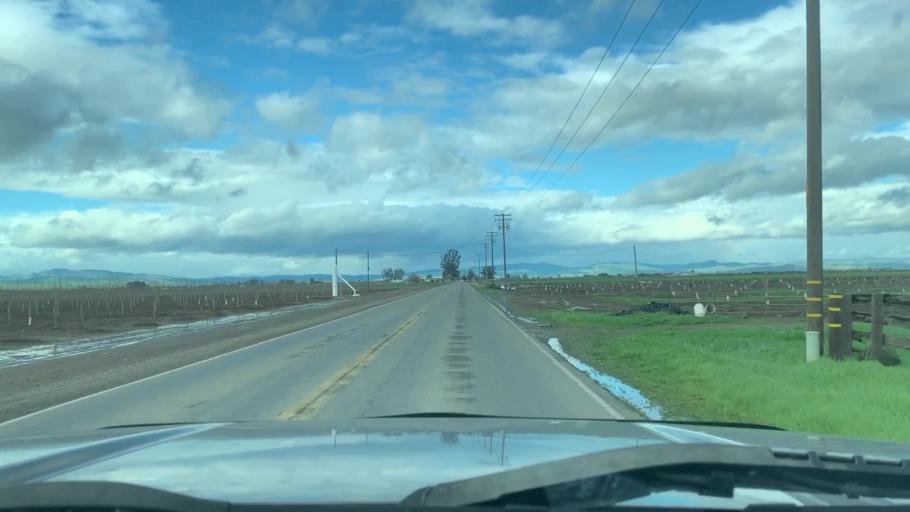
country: US
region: California
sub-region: Merced County
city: Los Banos
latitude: 37.0998
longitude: -120.8429
